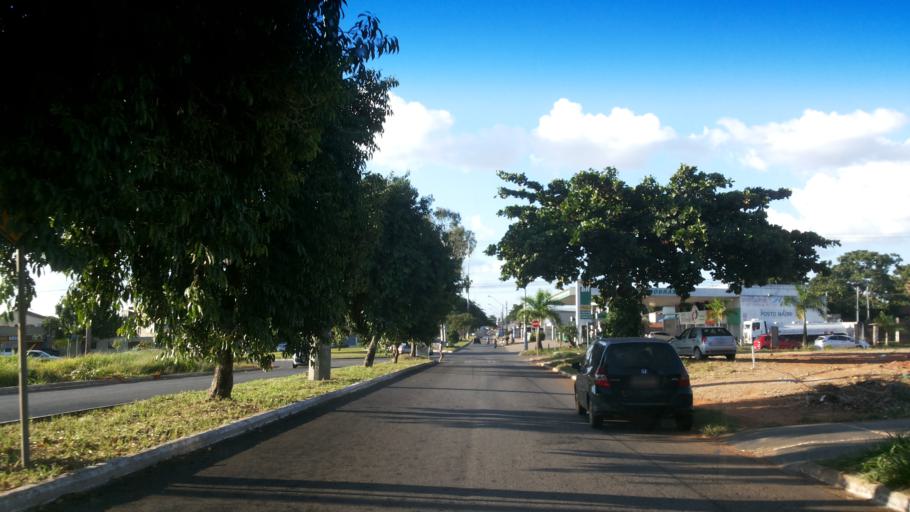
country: BR
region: Goias
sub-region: Goiania
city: Goiania
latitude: -16.7325
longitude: -49.3086
